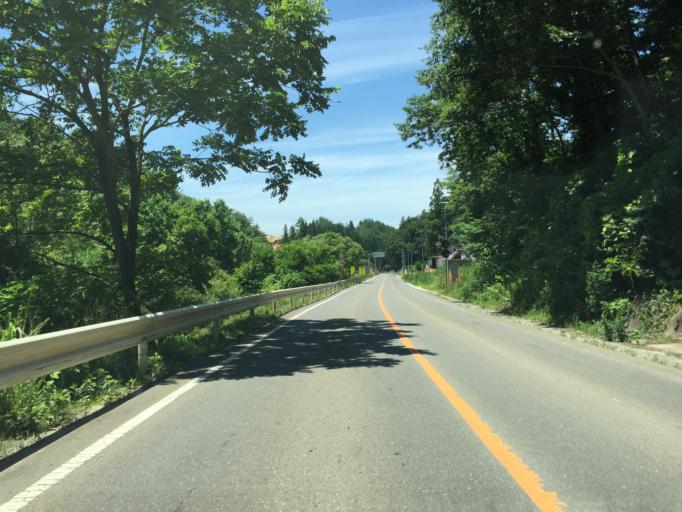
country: JP
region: Fukushima
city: Yanagawamachi-saiwaicho
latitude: 37.7554
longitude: 140.7103
